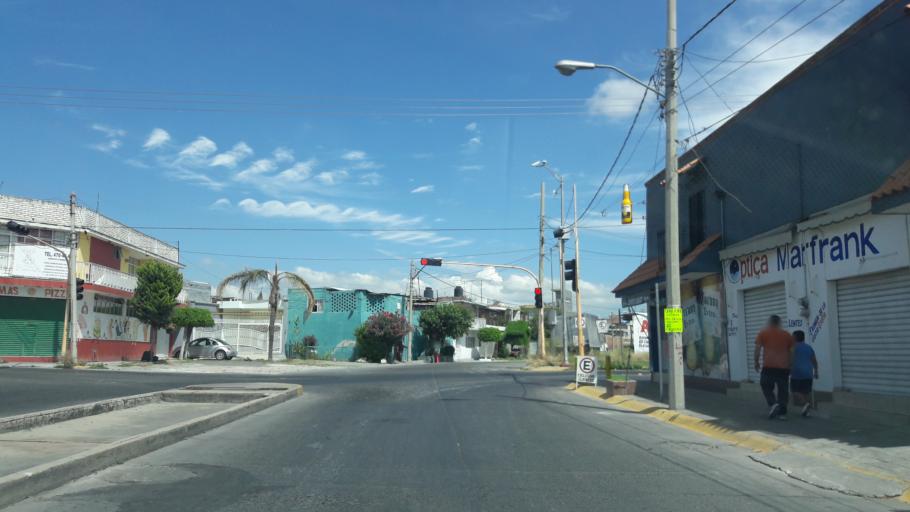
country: MX
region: Guanajuato
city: Leon
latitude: 21.1098
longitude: -101.7017
